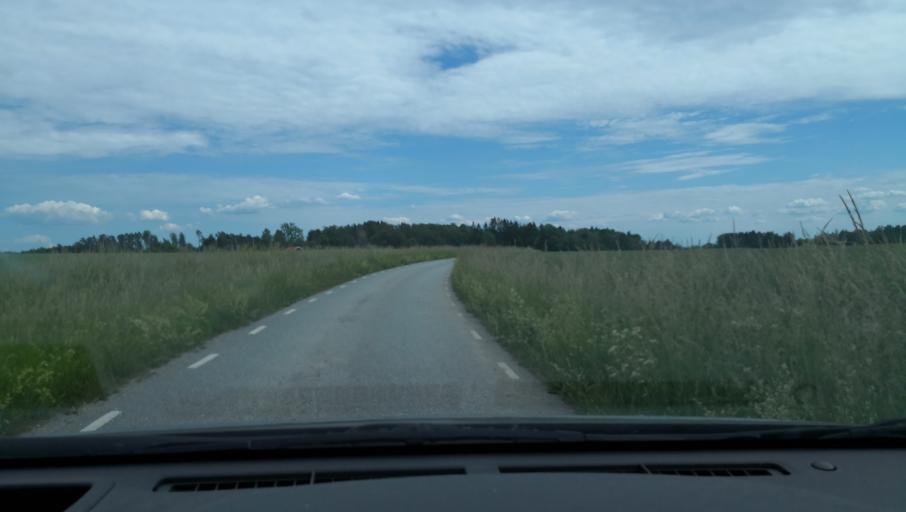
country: SE
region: Uppsala
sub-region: Habo Kommun
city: Balsta
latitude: 59.6930
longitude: 17.4572
